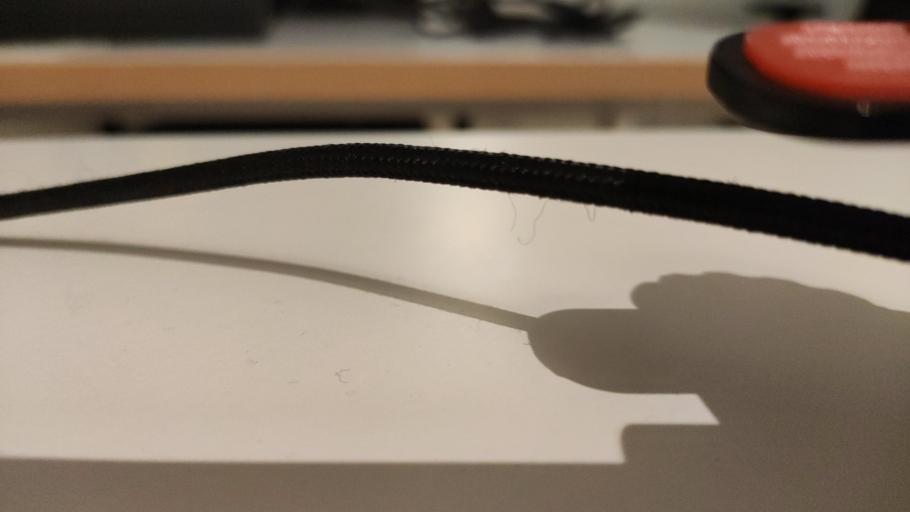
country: RU
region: Moskovskaya
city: Novosin'kovo
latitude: 56.3997
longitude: 37.2599
